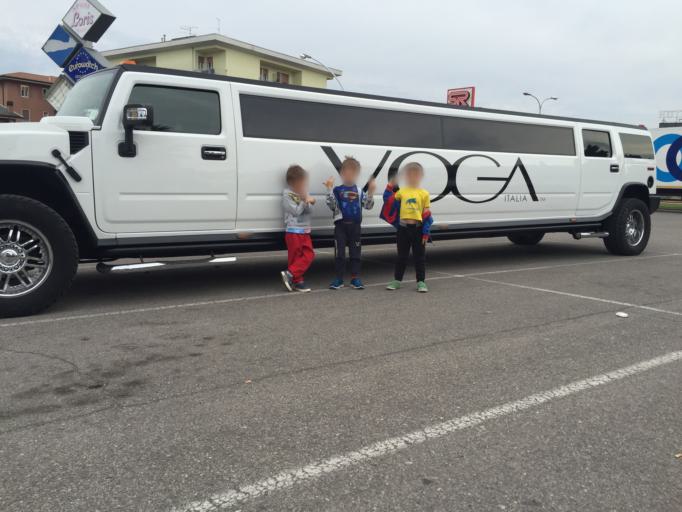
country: IT
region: Veneto
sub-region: Provincia di Verona
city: Bussolengo
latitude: 45.4691
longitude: 10.8540
